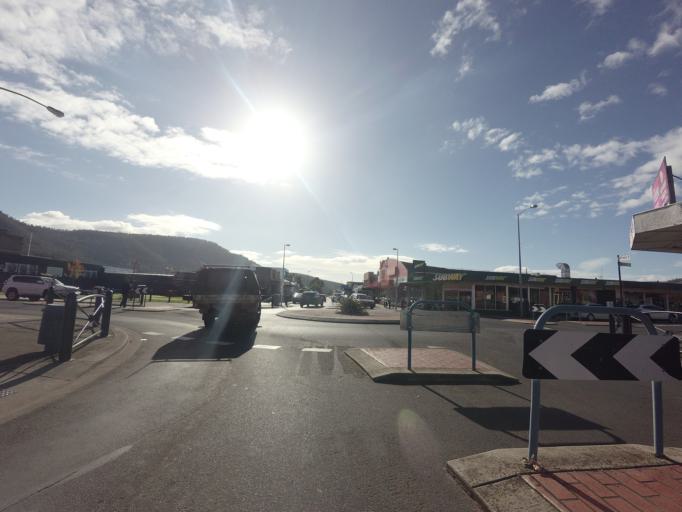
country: AU
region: Tasmania
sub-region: Derwent Valley
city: New Norfolk
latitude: -42.7812
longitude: 147.0620
